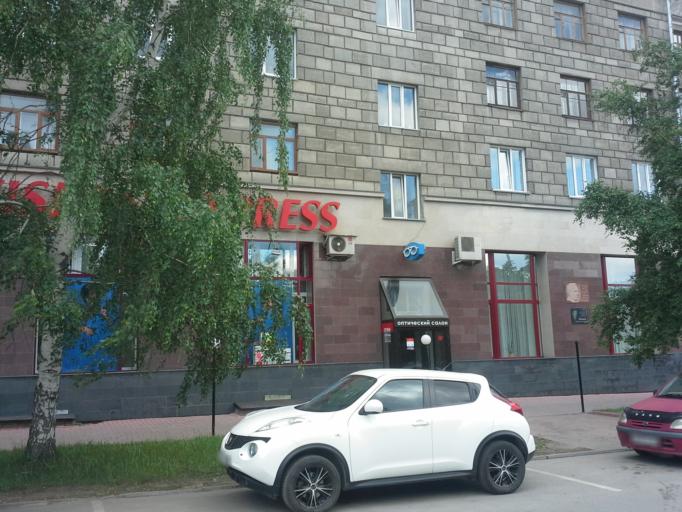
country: RU
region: Novosibirsk
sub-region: Novosibirskiy Rayon
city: Novosibirsk
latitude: 55.0292
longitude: 82.9225
